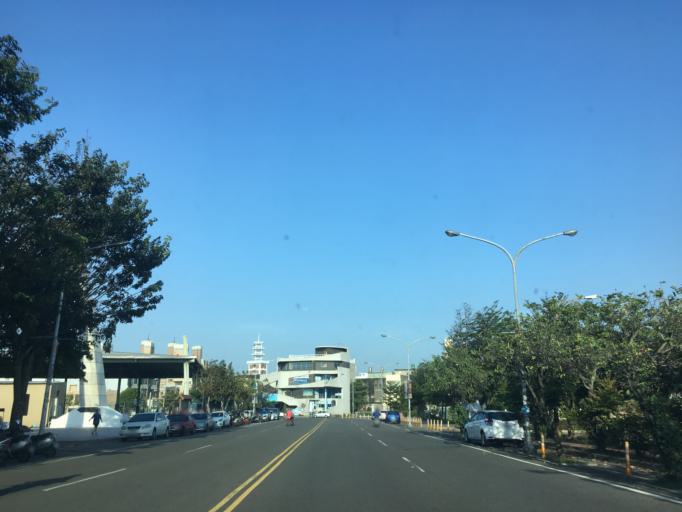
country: TW
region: Taiwan
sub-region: Changhua
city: Chang-hua
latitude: 24.0597
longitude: 120.4347
